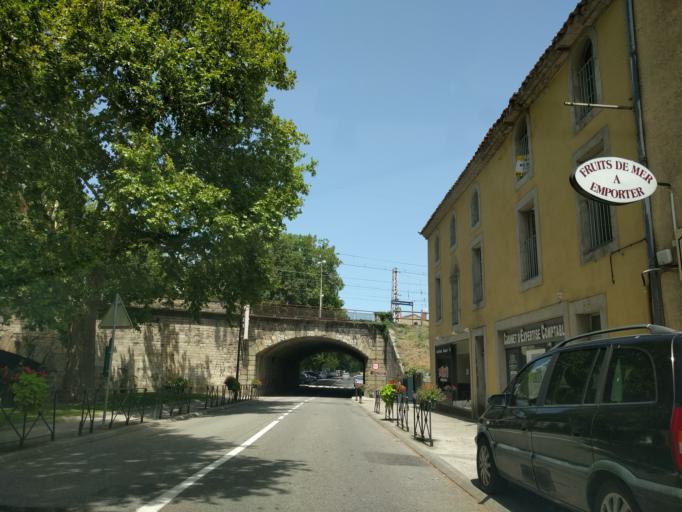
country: FR
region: Languedoc-Roussillon
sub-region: Departement de l'Aude
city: Carcassonne
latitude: 43.2179
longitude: 2.3537
